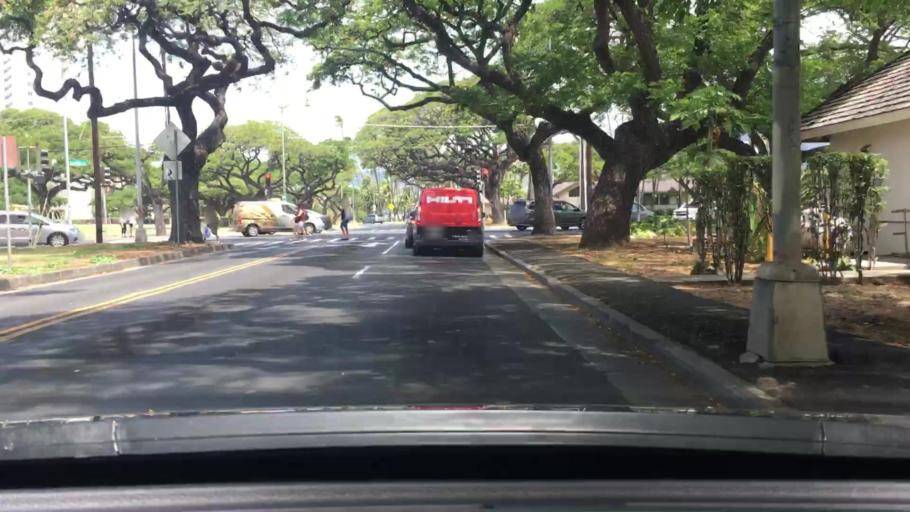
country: US
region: Hawaii
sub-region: Honolulu County
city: Honolulu
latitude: 21.2728
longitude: -157.8166
